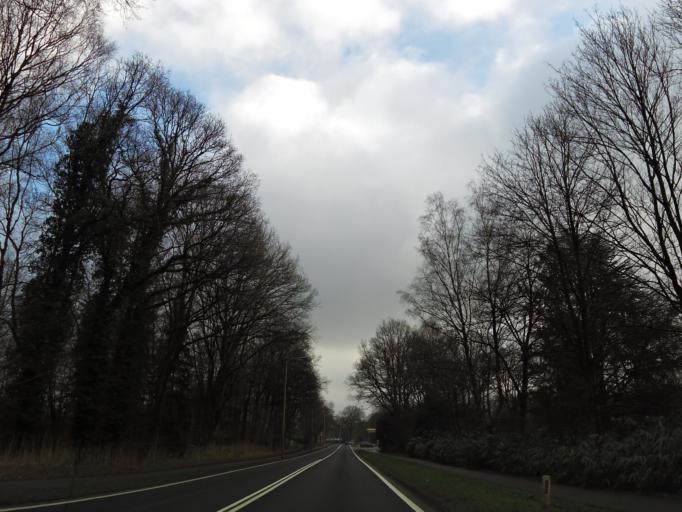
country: NL
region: Gelderland
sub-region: Gemeente Groesbeek
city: Bredeweg
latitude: 51.7379
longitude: 5.9249
